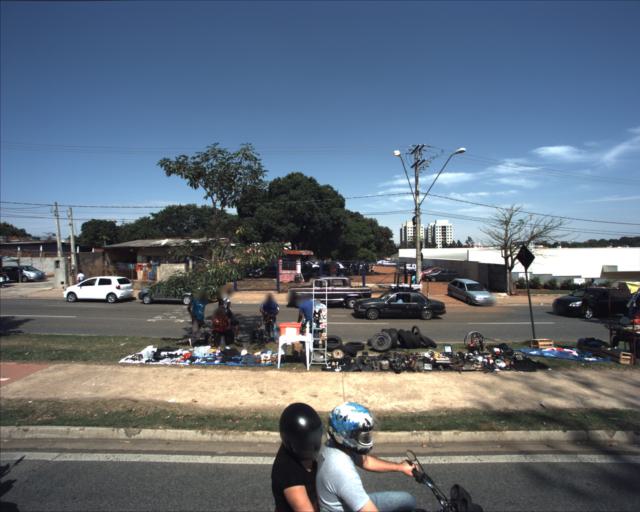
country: BR
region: Sao Paulo
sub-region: Sorocaba
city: Sorocaba
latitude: -23.4472
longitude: -47.5036
